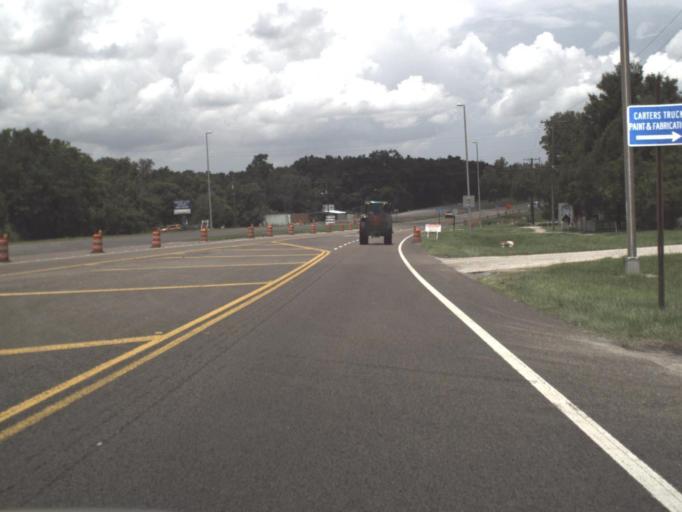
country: US
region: Florida
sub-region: Hillsborough County
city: Temple Terrace
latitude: 28.0380
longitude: -82.3491
